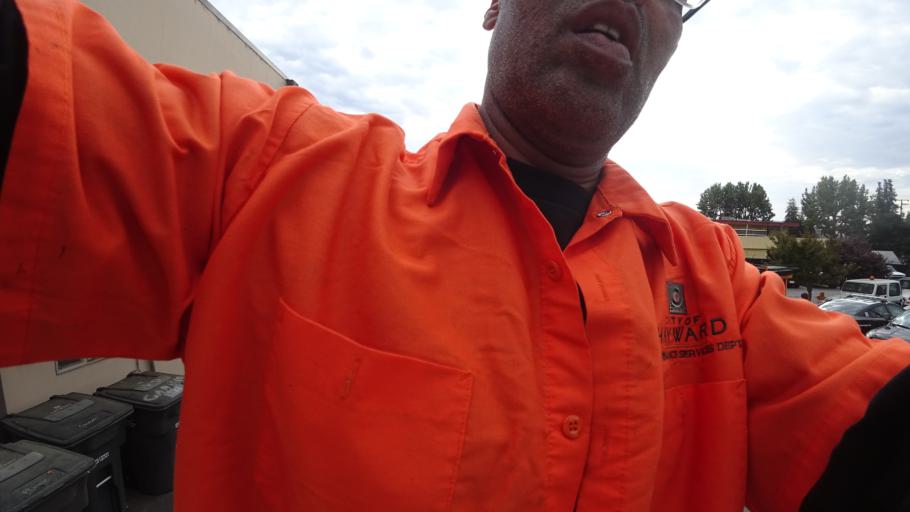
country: US
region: California
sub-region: Alameda County
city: Hayward
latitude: 37.6581
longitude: -122.0881
